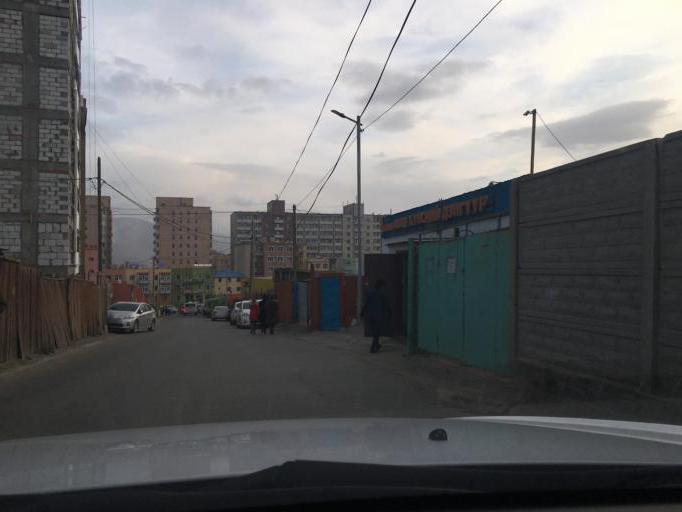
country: MN
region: Ulaanbaatar
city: Ulaanbaatar
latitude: 47.9226
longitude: 106.8574
